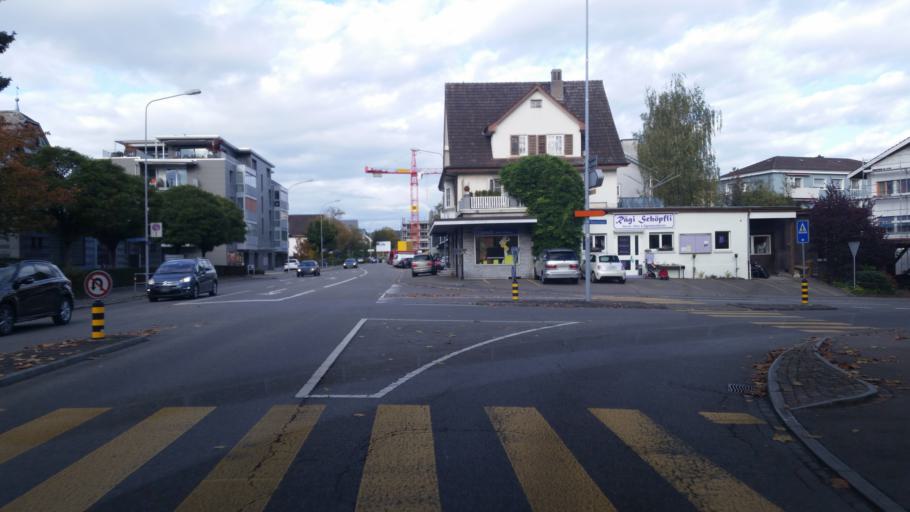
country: CH
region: Zurich
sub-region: Bezirk Dielsdorf
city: Regensdorf
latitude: 47.4325
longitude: 8.4673
